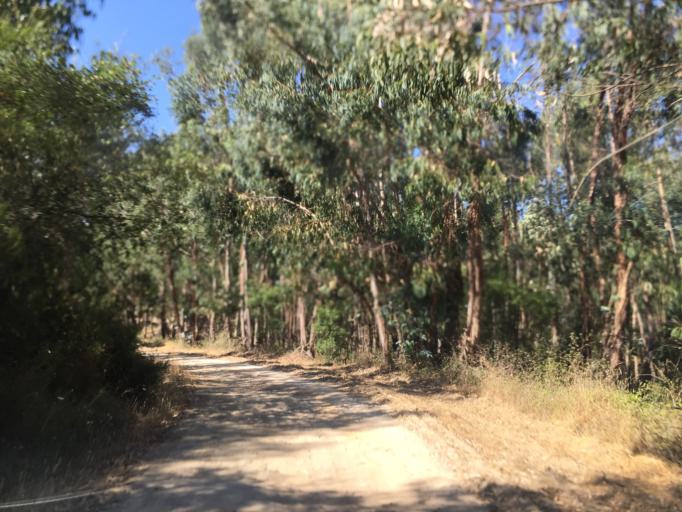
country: PT
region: Santarem
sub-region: Tomar
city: Tomar
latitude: 39.6139
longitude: -8.3530
